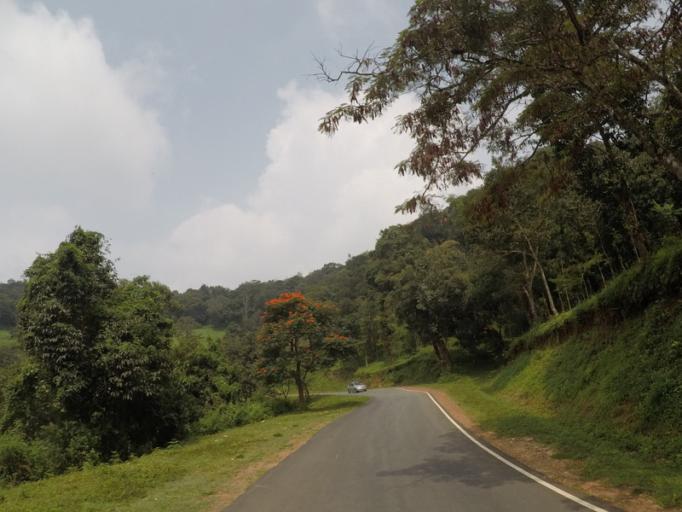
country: IN
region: Karnataka
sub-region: Chikmagalur
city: Mudigere
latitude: 13.1889
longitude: 75.4182
